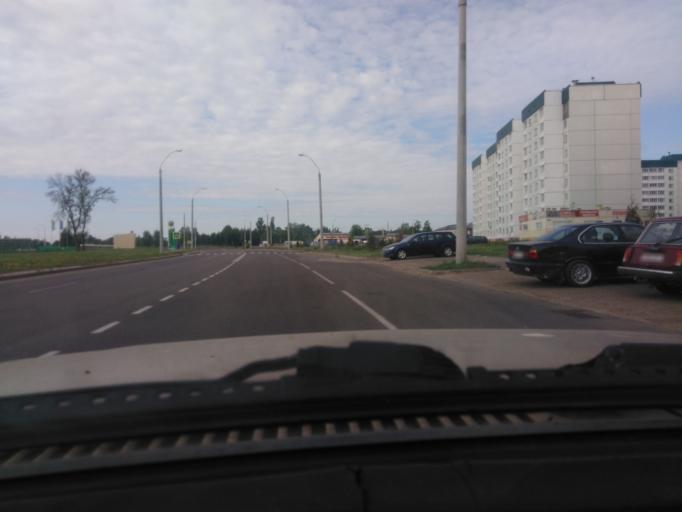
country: BY
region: Mogilev
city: Mahilyow
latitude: 53.9131
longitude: 30.2857
